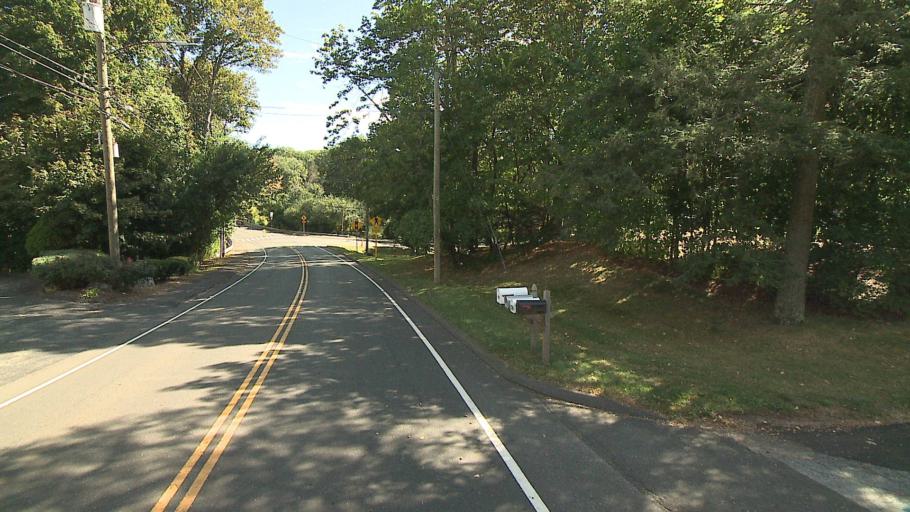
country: US
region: Connecticut
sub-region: Fairfield County
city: New Canaan
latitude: 41.1475
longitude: -73.4848
